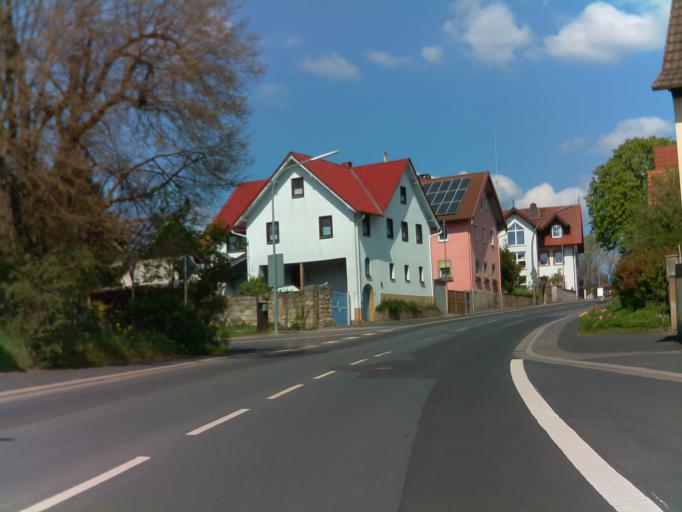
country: DE
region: Bavaria
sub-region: Regierungsbezirk Unterfranken
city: Sulzfeld
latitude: 50.2757
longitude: 10.4014
